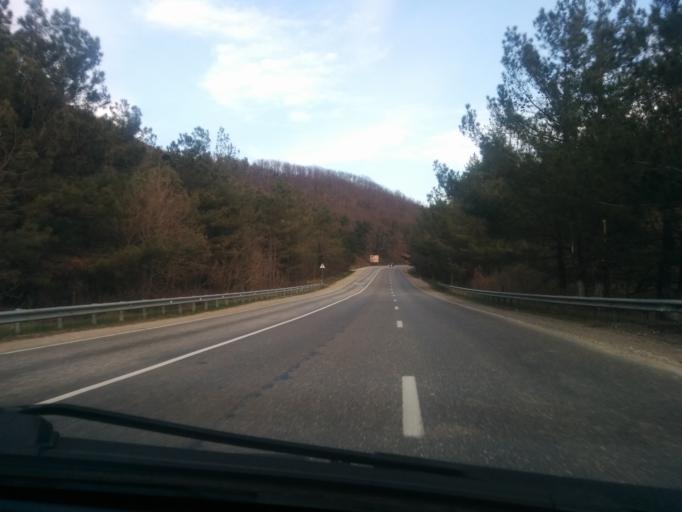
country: RU
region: Krasnodarskiy
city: Ol'ginka
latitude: 44.1824
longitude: 38.9290
